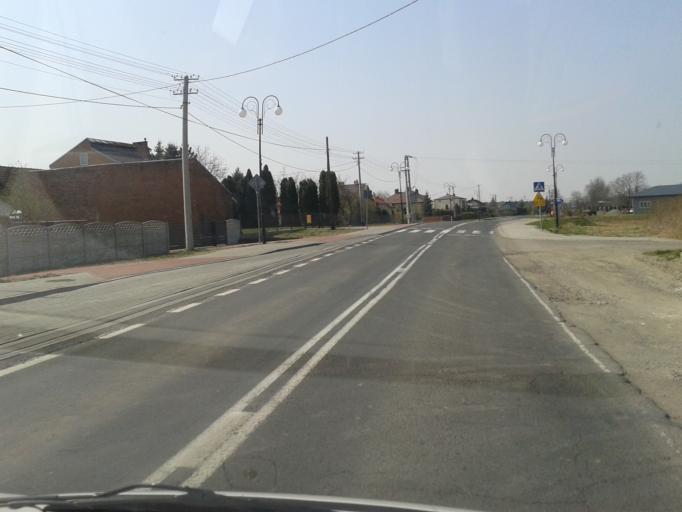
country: PL
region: Subcarpathian Voivodeship
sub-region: Powiat jaroslawski
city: Laszki
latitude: 50.0774
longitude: 22.8484
